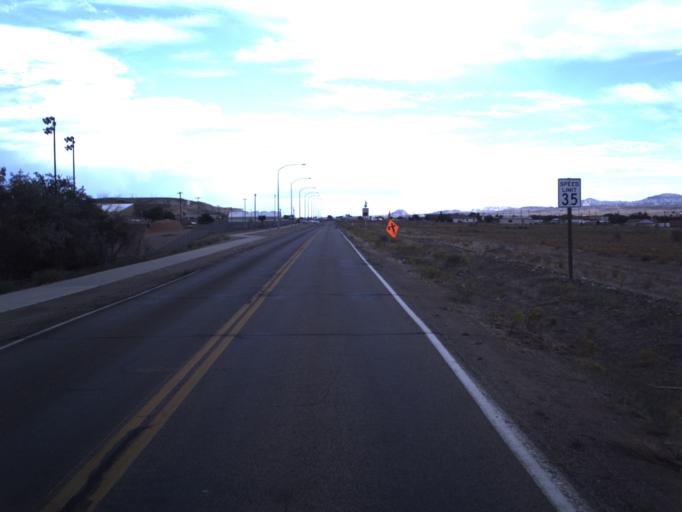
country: US
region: Utah
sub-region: San Juan County
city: Blanding
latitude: 37.2672
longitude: -109.3156
